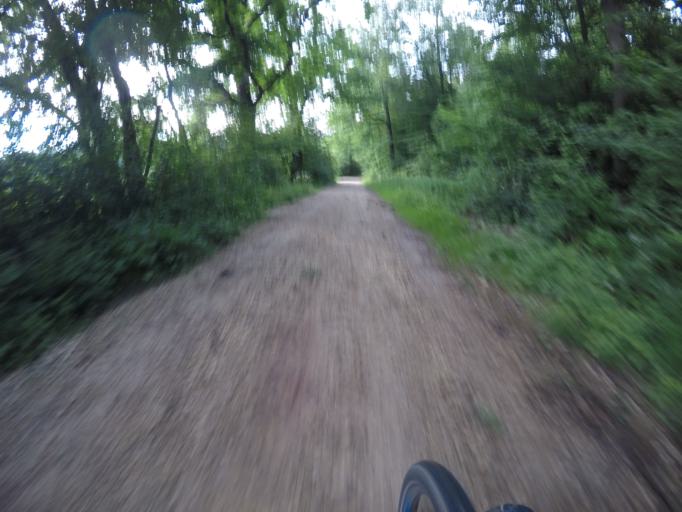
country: DE
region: Baden-Wuerttemberg
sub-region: Regierungsbezirk Stuttgart
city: Schlaitdorf
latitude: 48.6136
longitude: 9.2125
